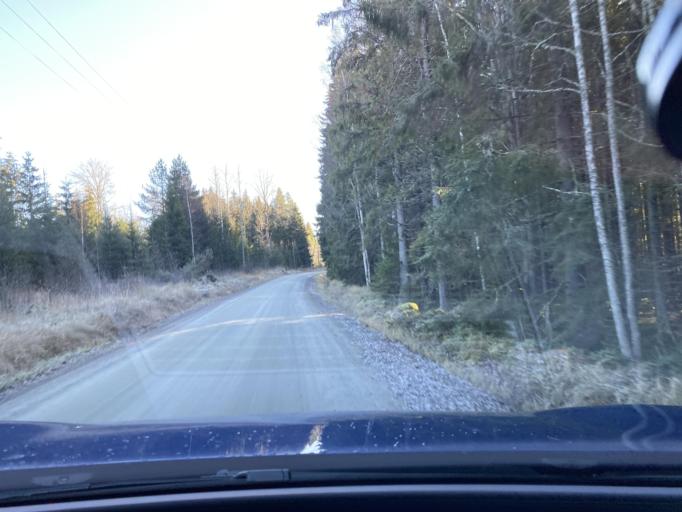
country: FI
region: Pirkanmaa
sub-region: Etelae-Pirkanmaa
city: Toijala
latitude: 61.0267
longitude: 23.8137
